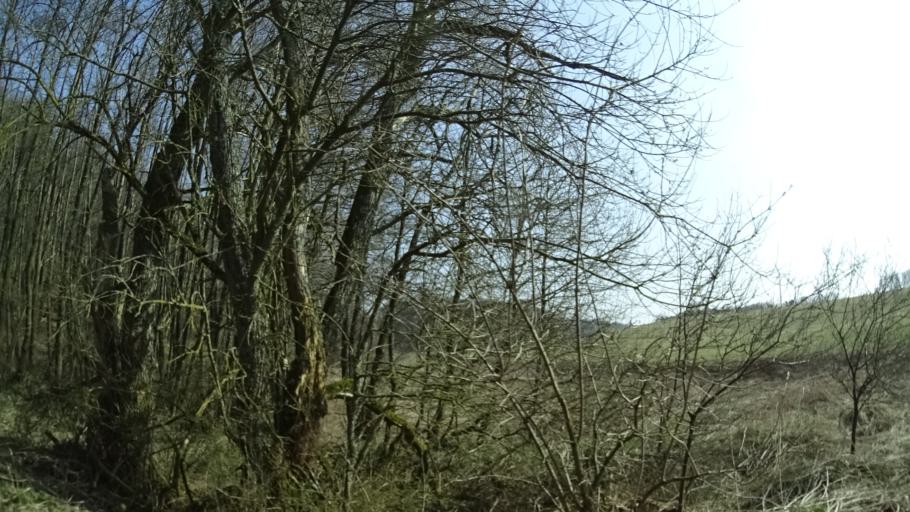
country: DE
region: Rheinland-Pfalz
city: Mettweiler
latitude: 49.5950
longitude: 7.3261
